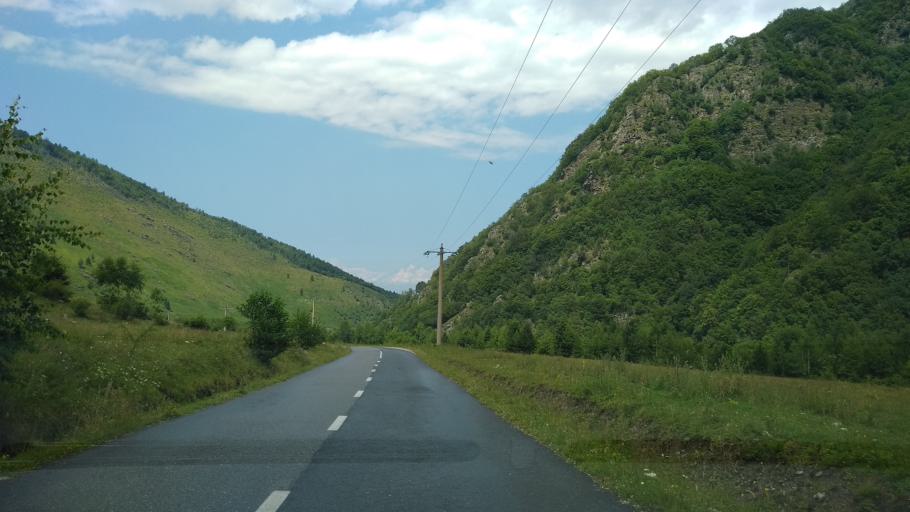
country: RO
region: Hunedoara
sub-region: Comuna Rau de Mori
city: Rau de Mori
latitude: 45.4603
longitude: 22.8982
